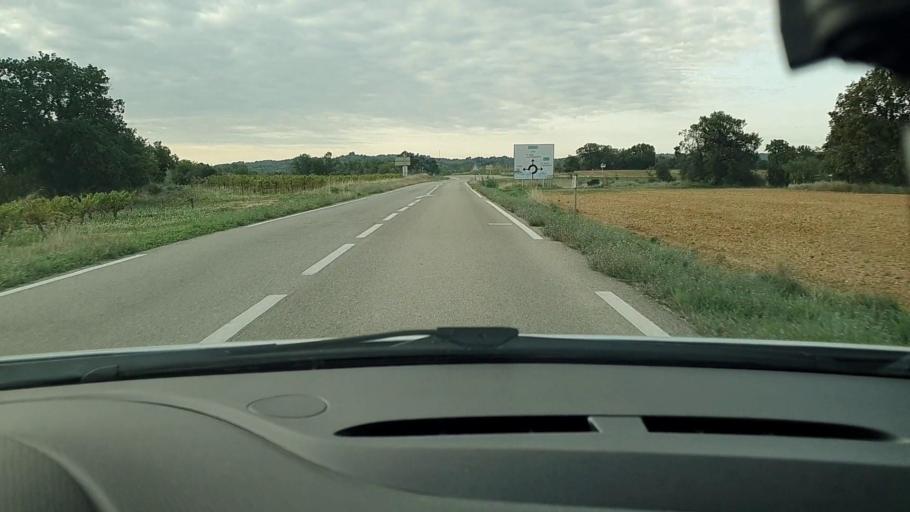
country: FR
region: Languedoc-Roussillon
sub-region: Departement du Gard
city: Mons
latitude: 44.0778
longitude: 4.2194
